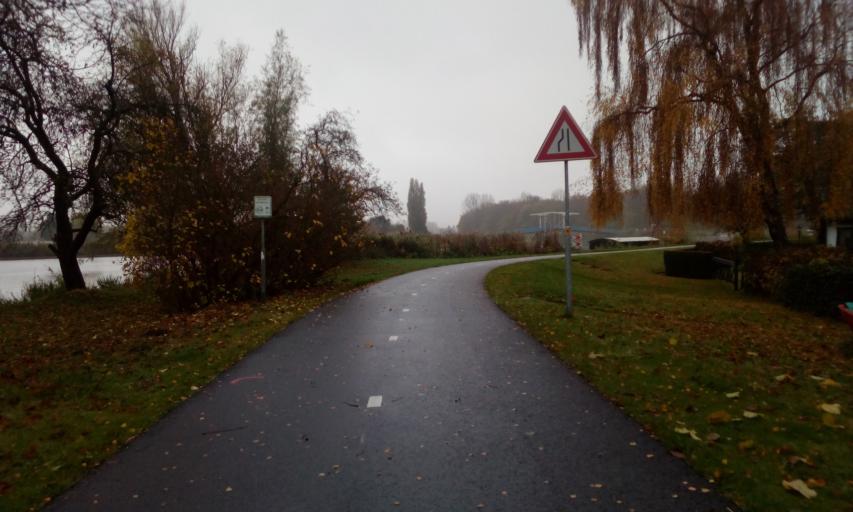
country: NL
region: South Holland
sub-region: Gemeente Lansingerland
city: Bleiswijk
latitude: 51.9929
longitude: 4.5475
